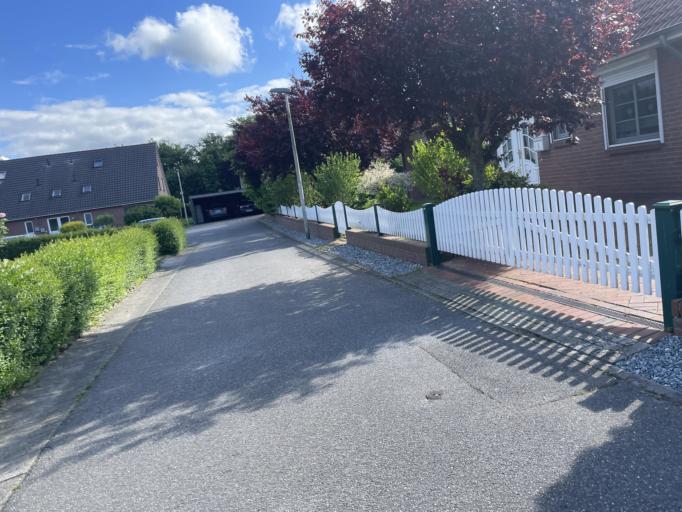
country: DE
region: Schleswig-Holstein
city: Mildstedt
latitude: 54.4656
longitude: 9.0973
